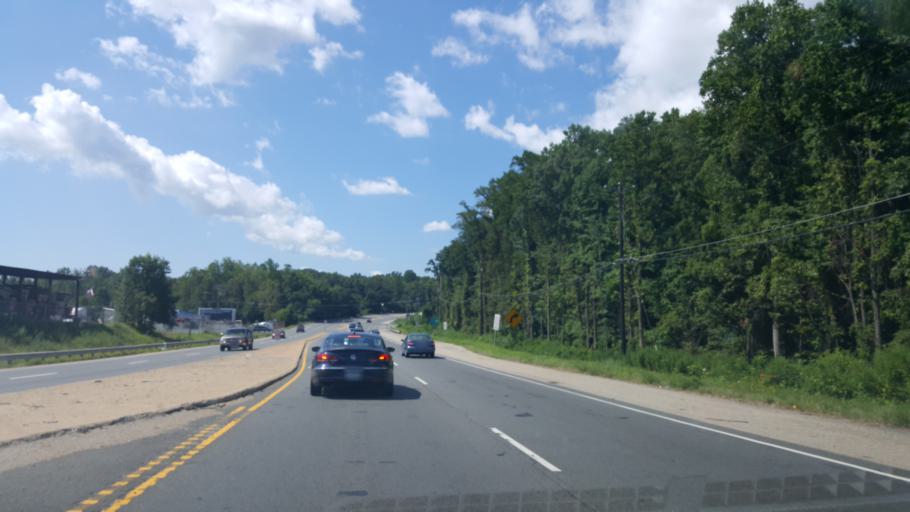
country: US
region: Virginia
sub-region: Fairfax County
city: Lorton
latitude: 38.6822
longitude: -77.2250
